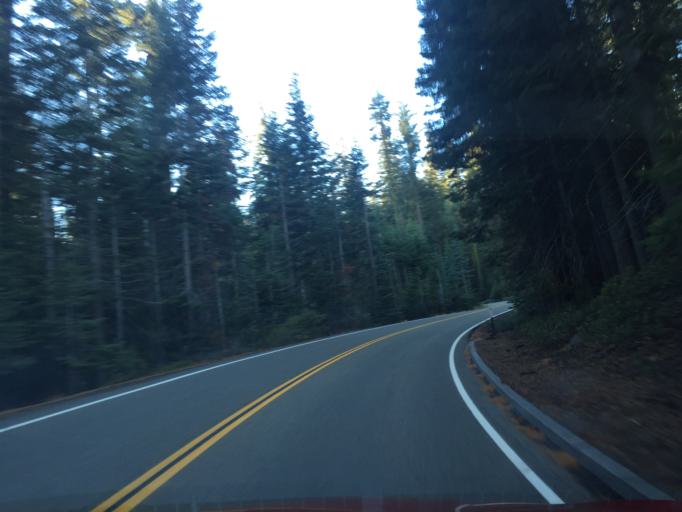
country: US
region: California
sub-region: Mariposa County
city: Yosemite Valley
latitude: 37.6736
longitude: -119.6891
